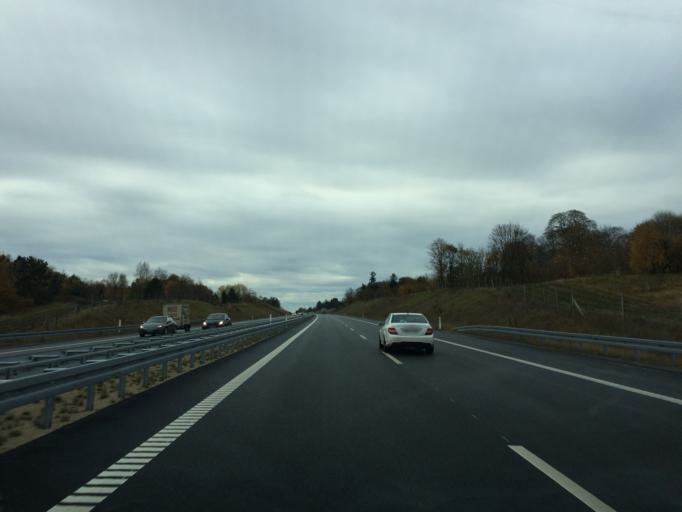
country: DK
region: Central Jutland
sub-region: Silkeborg Kommune
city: Silkeborg
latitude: 56.1808
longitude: 9.4835
